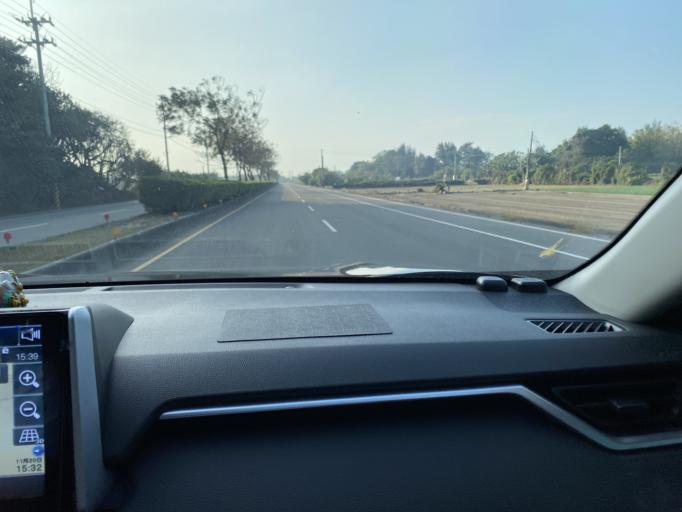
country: TW
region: Taiwan
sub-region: Changhua
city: Chang-hua
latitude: 23.9603
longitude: 120.3947
